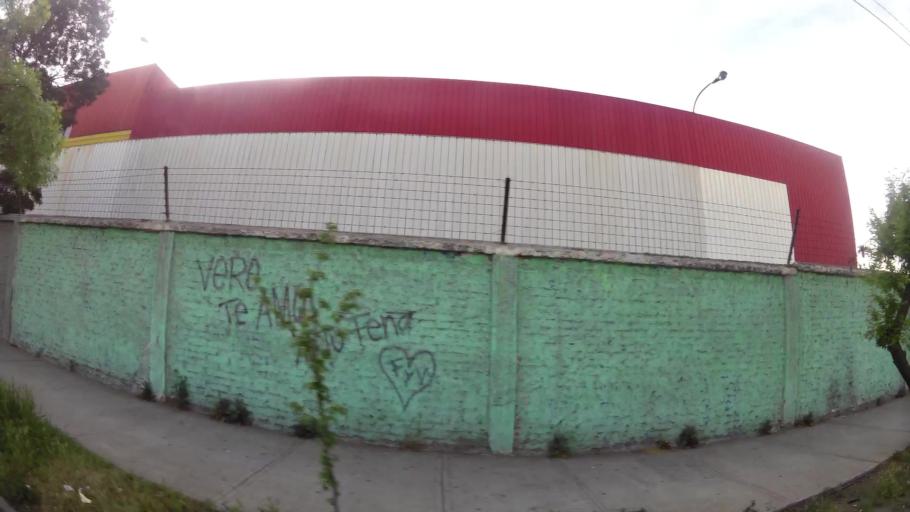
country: CL
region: Santiago Metropolitan
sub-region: Provincia de Santiago
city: Santiago
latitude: -33.5234
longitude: -70.6768
